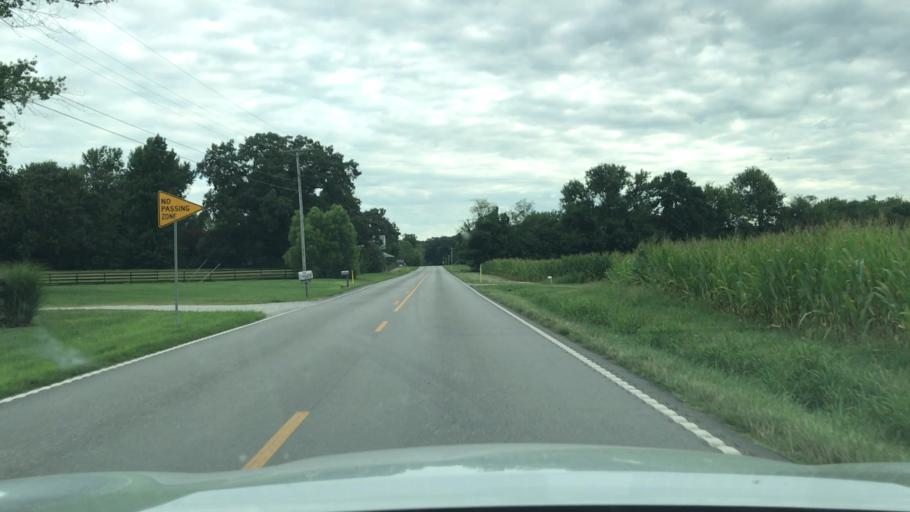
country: US
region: Kentucky
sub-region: Todd County
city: Guthrie
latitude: 36.7194
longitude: -87.1910
